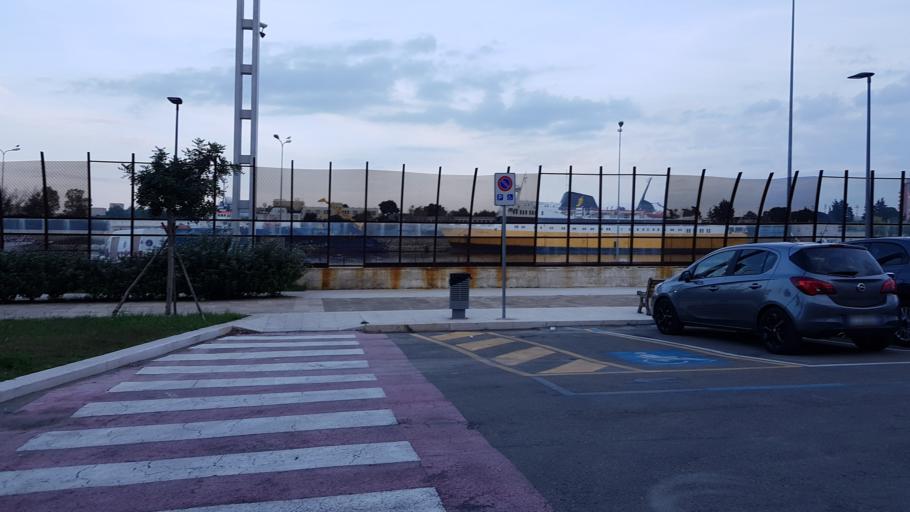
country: IT
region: Apulia
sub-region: Provincia di Brindisi
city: Brindisi
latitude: 40.6367
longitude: 17.9495
